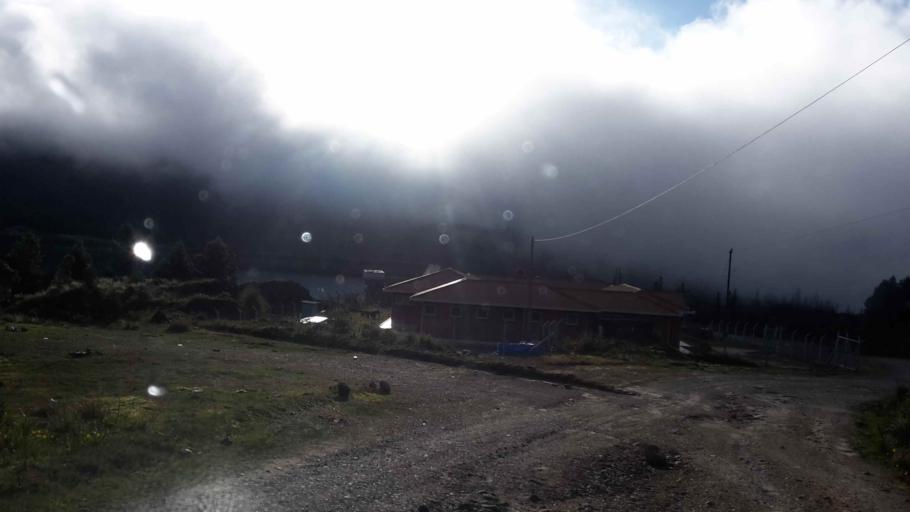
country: BO
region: Cochabamba
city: Colomi
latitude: -17.2270
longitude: -65.8893
